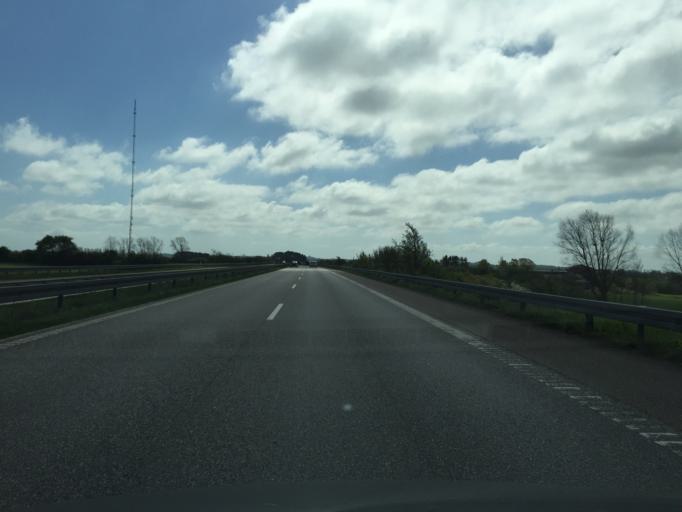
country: DK
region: Zealand
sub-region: Vordingborg Kommune
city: Orslev
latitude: 55.0590
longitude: 11.9725
